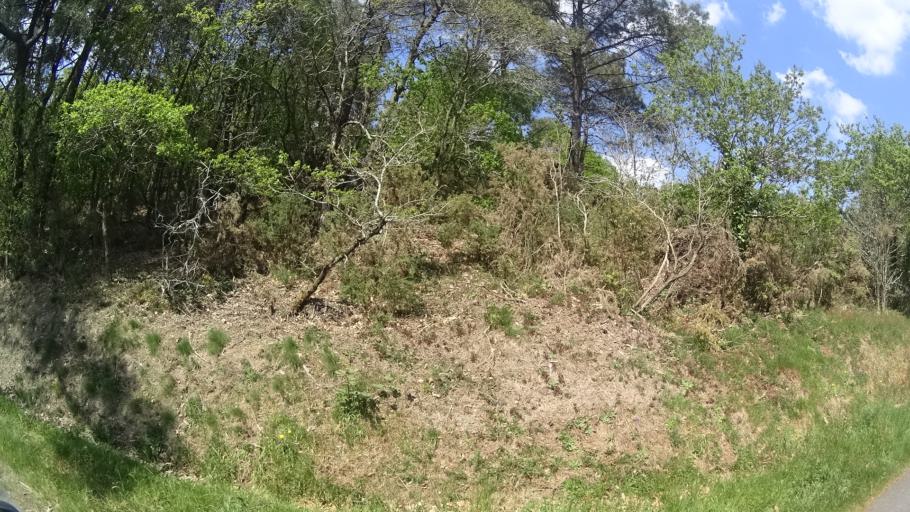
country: FR
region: Brittany
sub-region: Departement du Morbihan
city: Beganne
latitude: 47.5983
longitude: -2.2017
